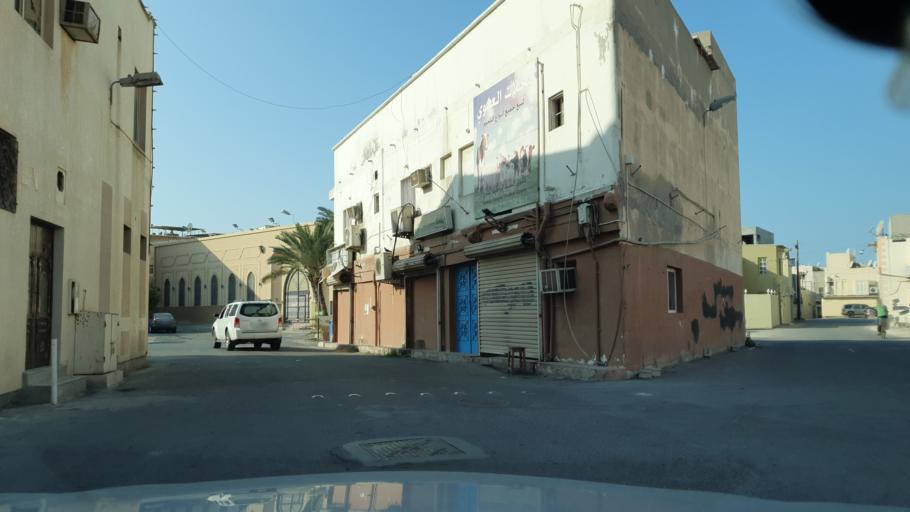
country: BH
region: Manama
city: Jidd Hafs
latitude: 26.2185
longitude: 50.4660
